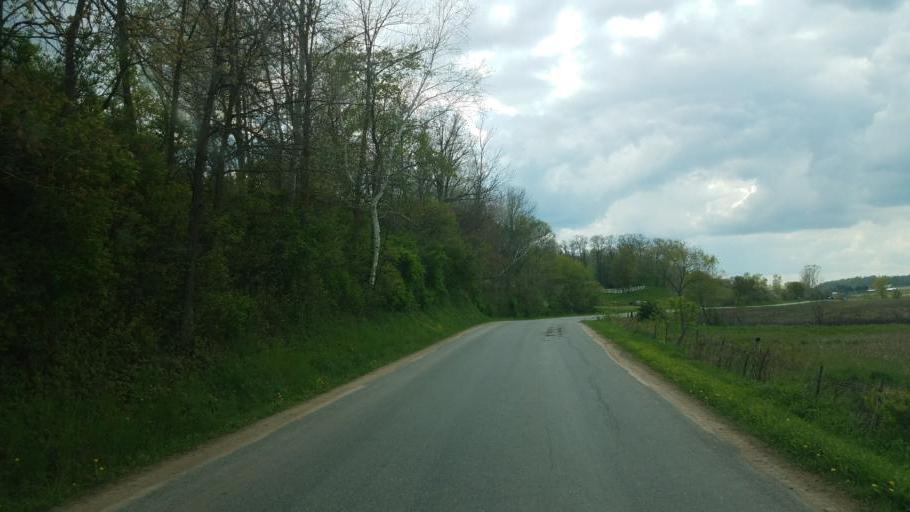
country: US
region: Wisconsin
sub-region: Vernon County
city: Hillsboro
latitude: 43.6207
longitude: -90.3712
